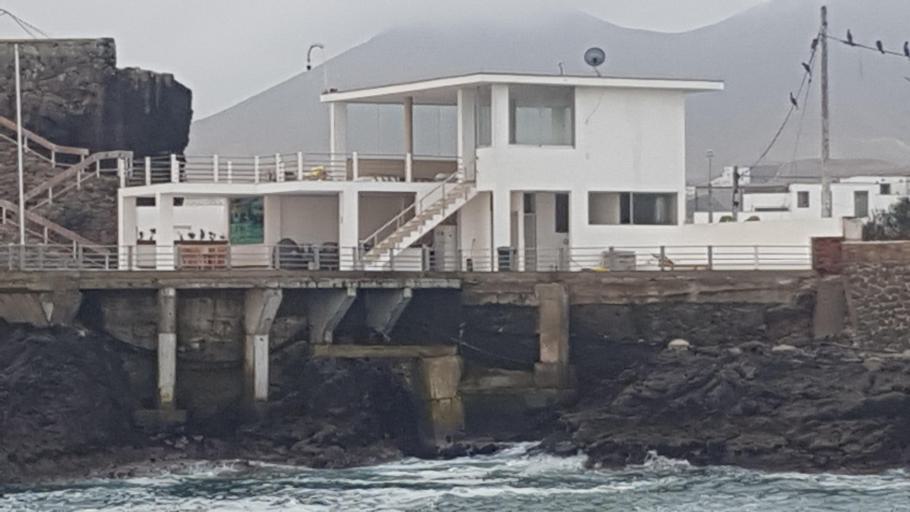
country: PE
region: Lima
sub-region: Lima
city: Pucusana
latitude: -12.4792
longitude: -76.8009
